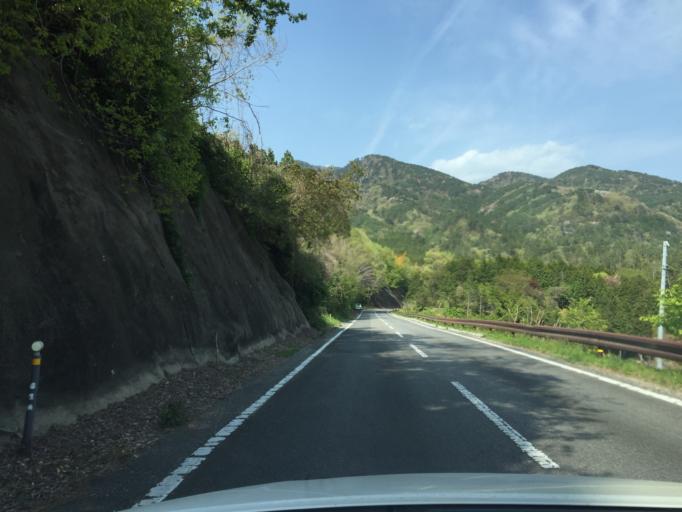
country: JP
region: Fukushima
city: Iwaki
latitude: 37.1558
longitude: 140.8578
